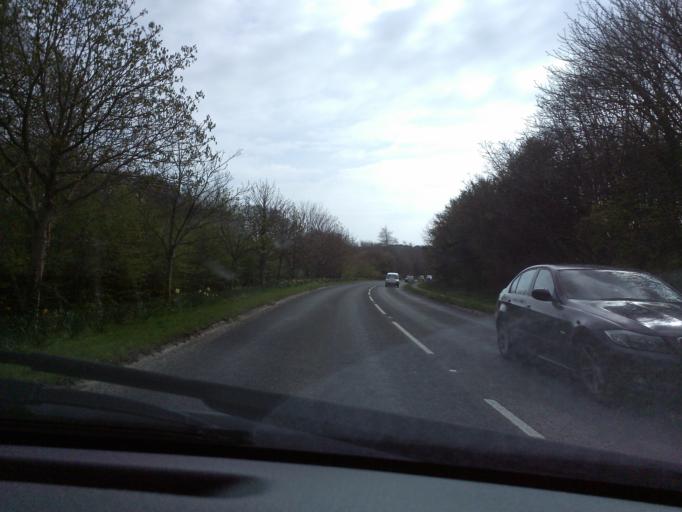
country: GB
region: England
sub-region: Cornwall
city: Penzance
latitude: 50.1222
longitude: -5.5504
